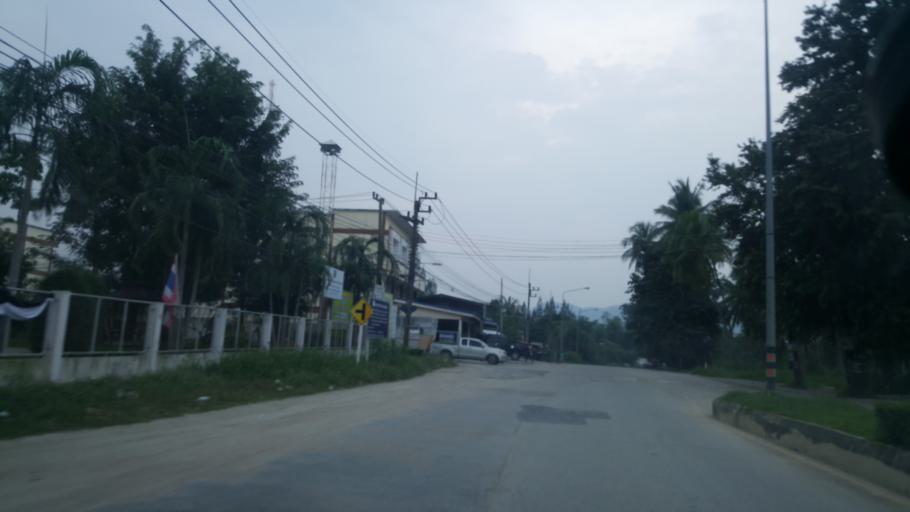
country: TH
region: Chon Buri
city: Si Racha
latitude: 13.2374
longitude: 101.0058
